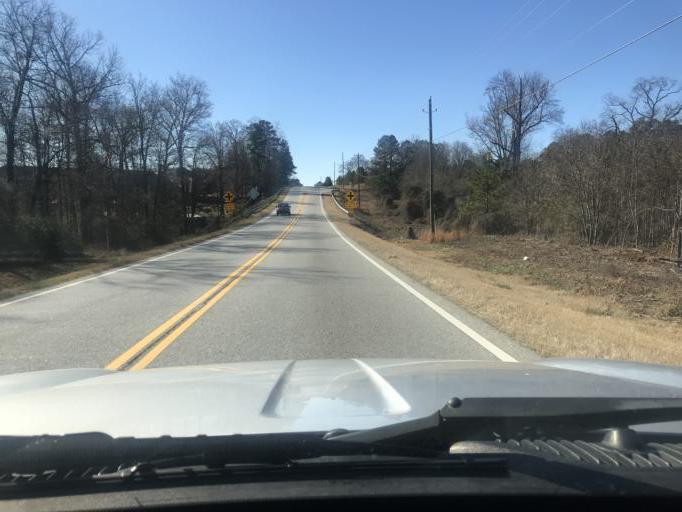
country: US
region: Georgia
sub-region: Barrow County
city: Winder
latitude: 33.9400
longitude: -83.7619
